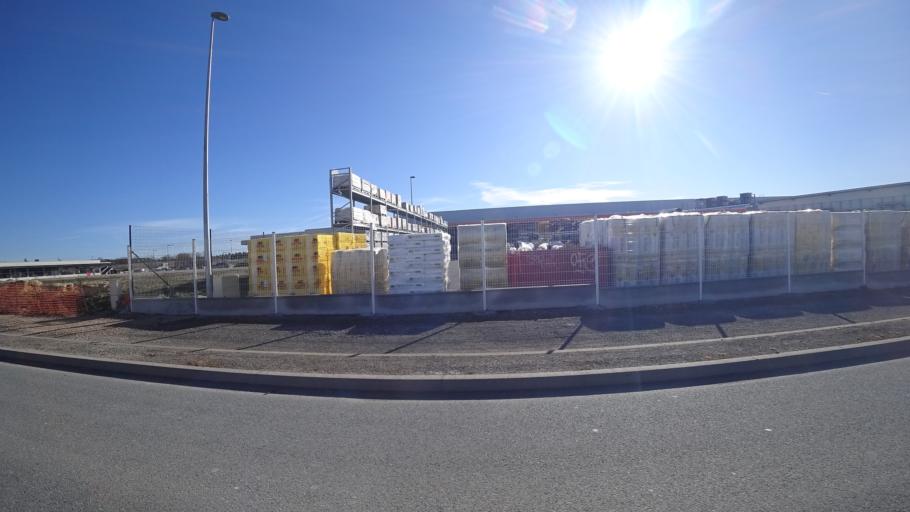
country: FR
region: Midi-Pyrenees
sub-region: Departement de l'Aveyron
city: Sebazac-Concoures
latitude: 44.3905
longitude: 2.5946
